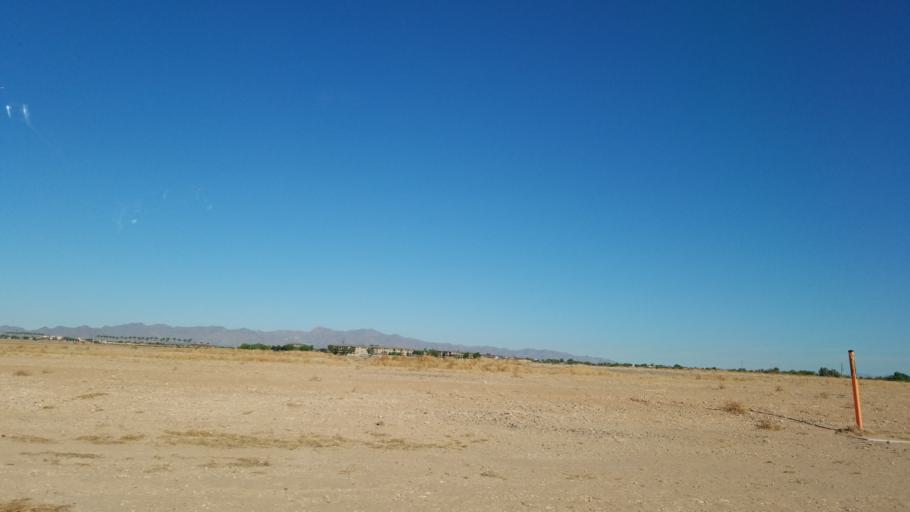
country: US
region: Arizona
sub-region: Maricopa County
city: Goodyear
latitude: 33.4316
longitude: -112.3802
